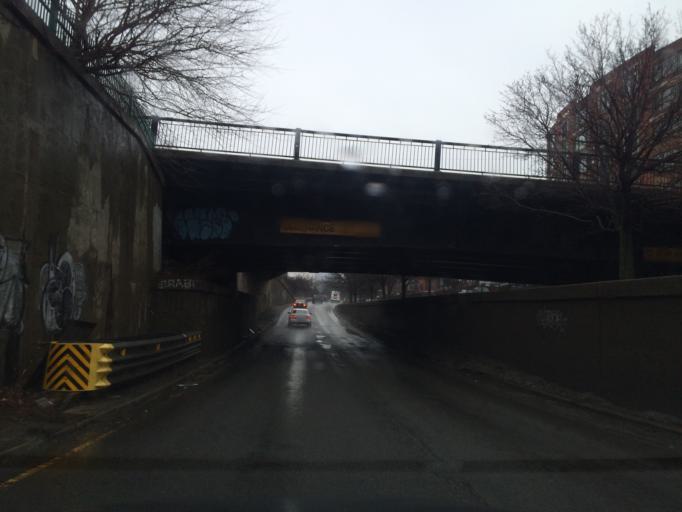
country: US
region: Massachusetts
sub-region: Middlesex County
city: Cambridge
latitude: 42.3514
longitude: -71.0906
